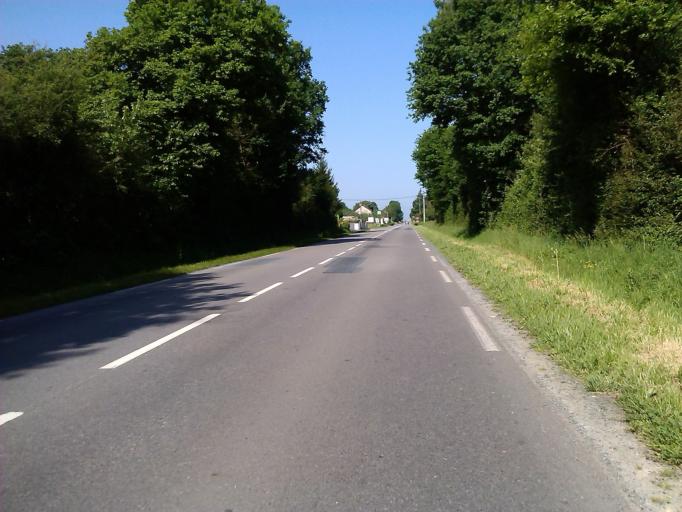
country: FR
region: Centre
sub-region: Departement de l'Indre
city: Neuvy-Saint-Sepulchre
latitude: 46.5982
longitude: 1.7906
